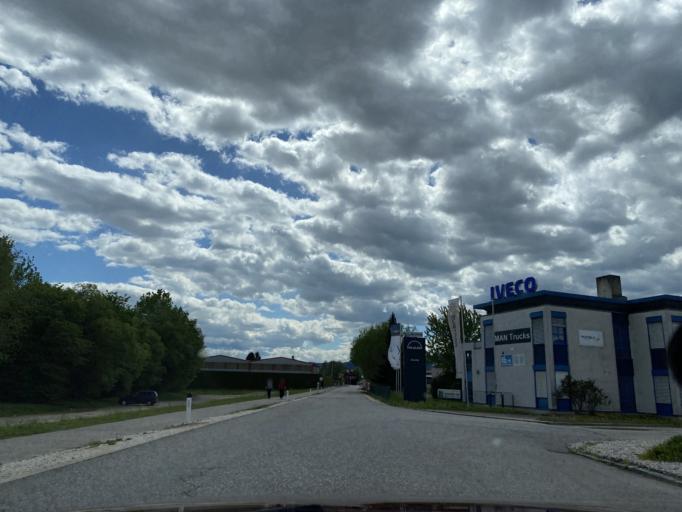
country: AT
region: Carinthia
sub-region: Politischer Bezirk Wolfsberg
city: Wolfsberg
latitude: 46.8341
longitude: 14.8390
